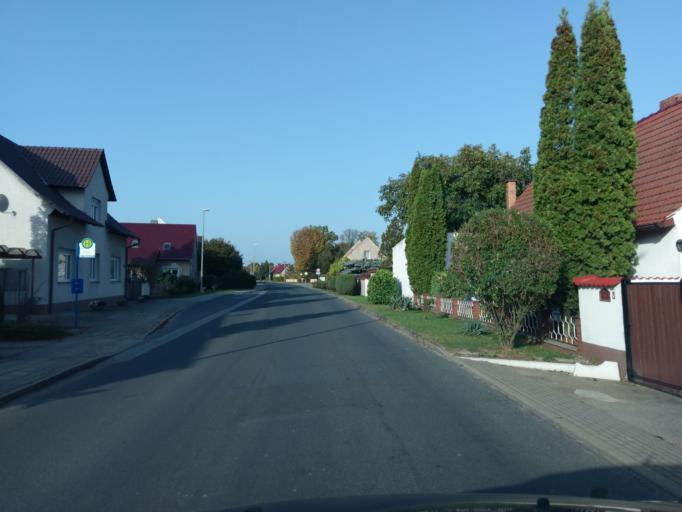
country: DE
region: Brandenburg
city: Falkenberg
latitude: 51.6361
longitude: 13.2362
